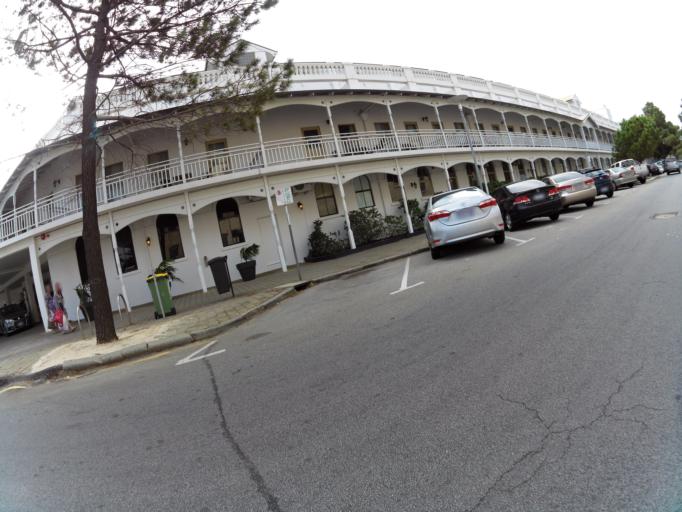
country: AU
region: Western Australia
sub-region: Fremantle
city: South Fremantle
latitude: -32.0577
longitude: 115.7465
